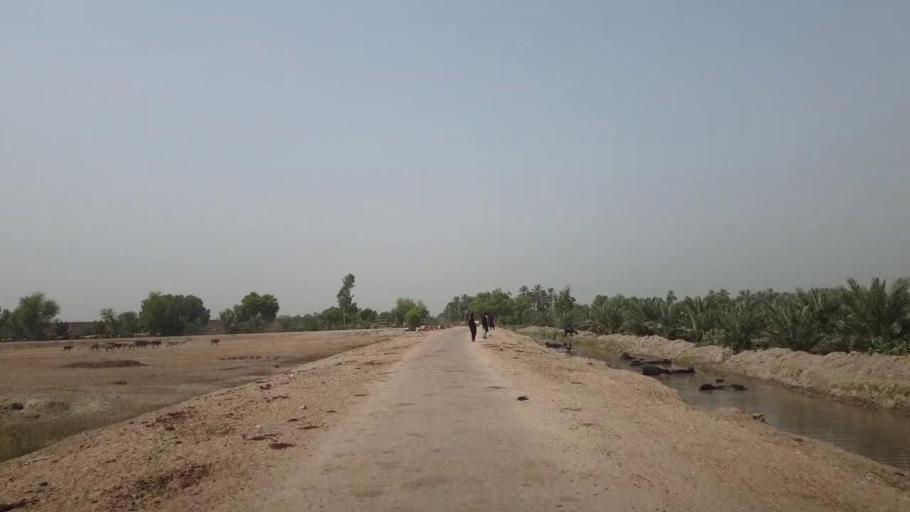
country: PK
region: Sindh
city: Gambat
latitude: 27.4026
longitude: 68.5532
